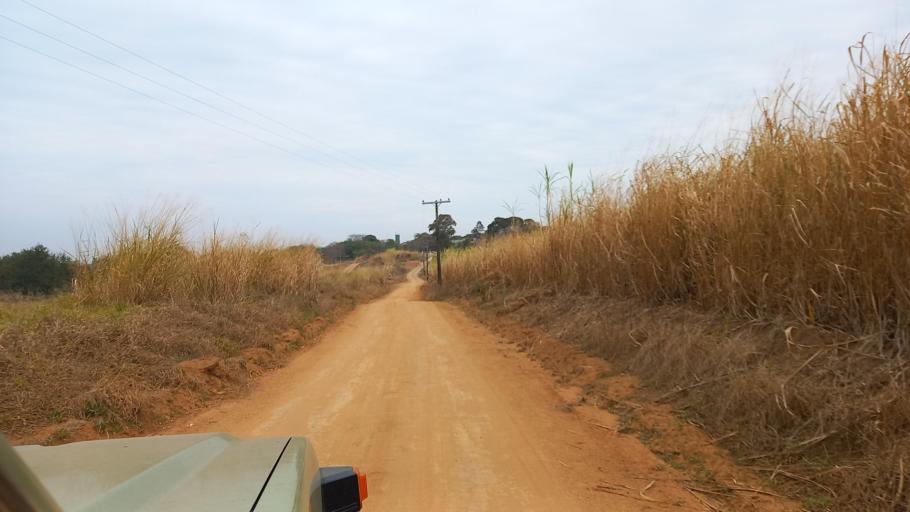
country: BR
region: Sao Paulo
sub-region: Moji-Guacu
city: Mogi-Gaucu
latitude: -22.2721
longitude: -46.8454
